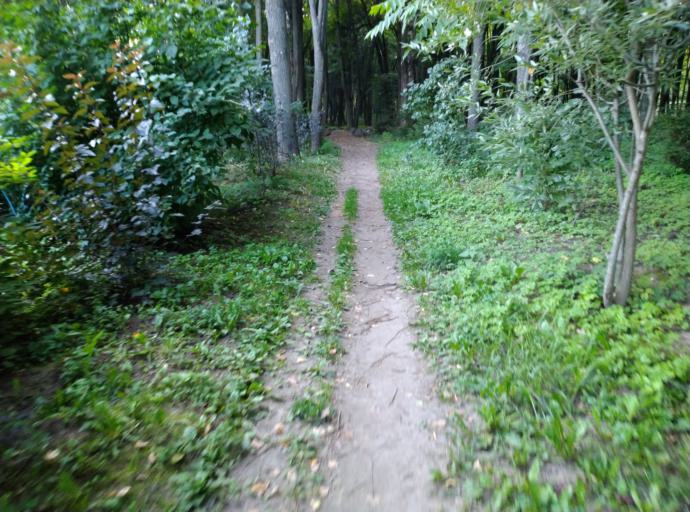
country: RU
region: Kostroma
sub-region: Kostromskoy Rayon
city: Kostroma
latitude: 57.7521
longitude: 40.9606
